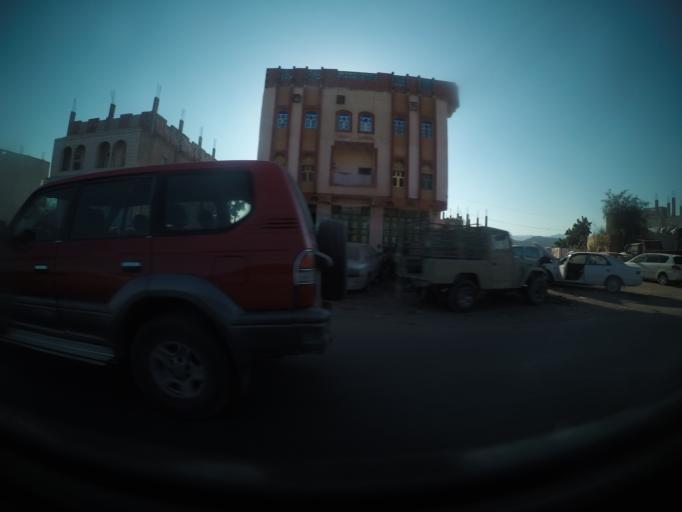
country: YE
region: Lahij
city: Habil ar Raydah
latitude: 13.6398
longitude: 44.8589
